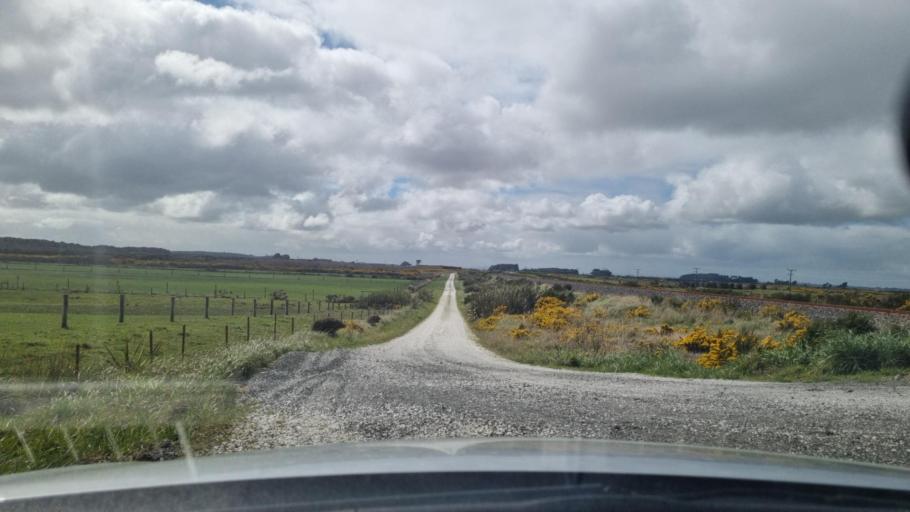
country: NZ
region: Southland
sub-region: Invercargill City
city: Bluff
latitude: -46.5353
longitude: 168.3040
